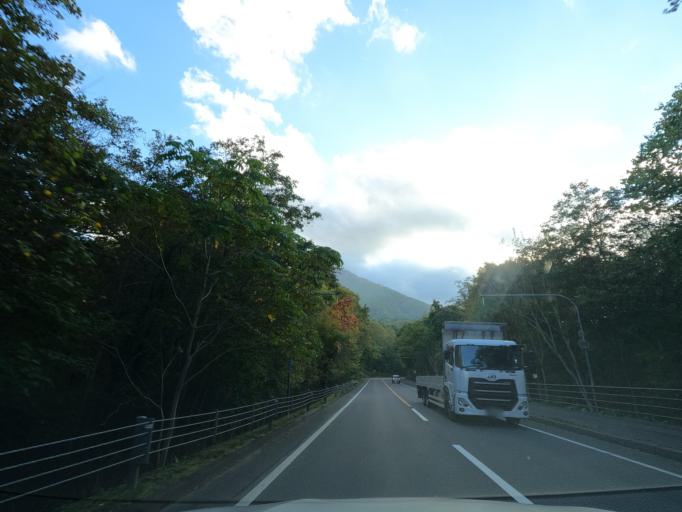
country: JP
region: Hokkaido
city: Shiraoi
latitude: 42.7356
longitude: 141.3774
